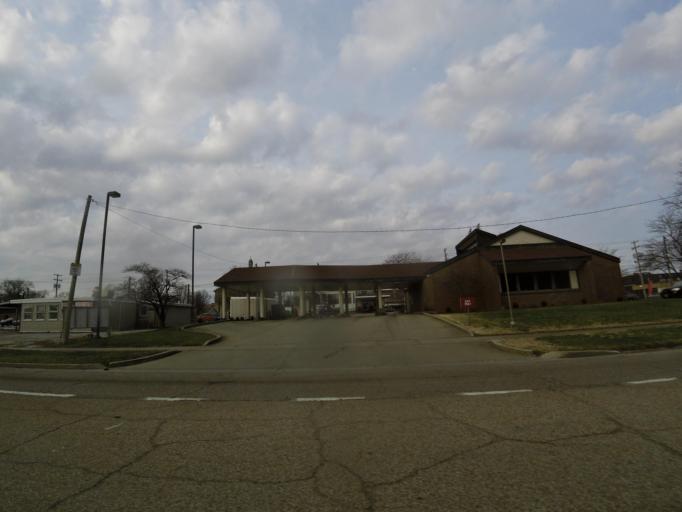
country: US
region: Illinois
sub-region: Christian County
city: Pana
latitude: 39.3868
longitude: -89.0809
